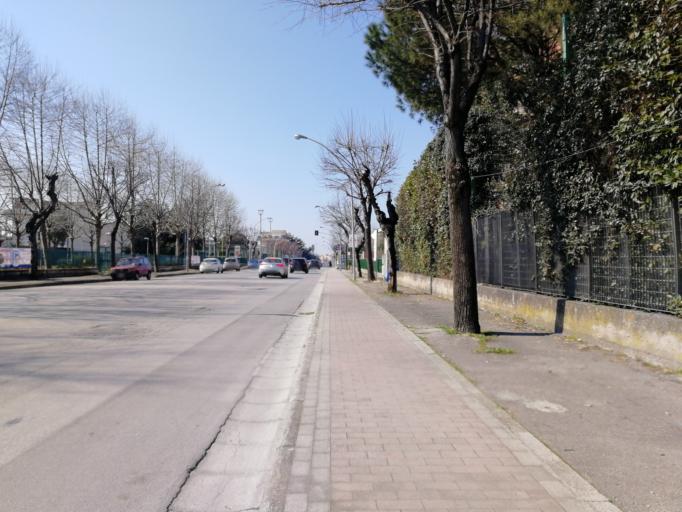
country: IT
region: Campania
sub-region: Provincia di Caserta
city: Santa Maria Capua Vetere
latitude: 41.0900
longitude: 14.2596
